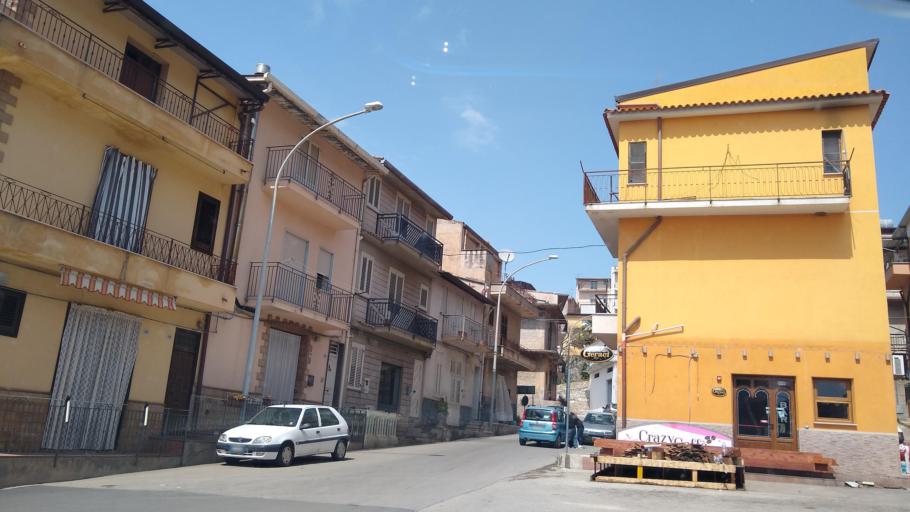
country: IT
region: Sicily
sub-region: Palermo
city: San Cipirello
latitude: 37.9678
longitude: 13.1786
